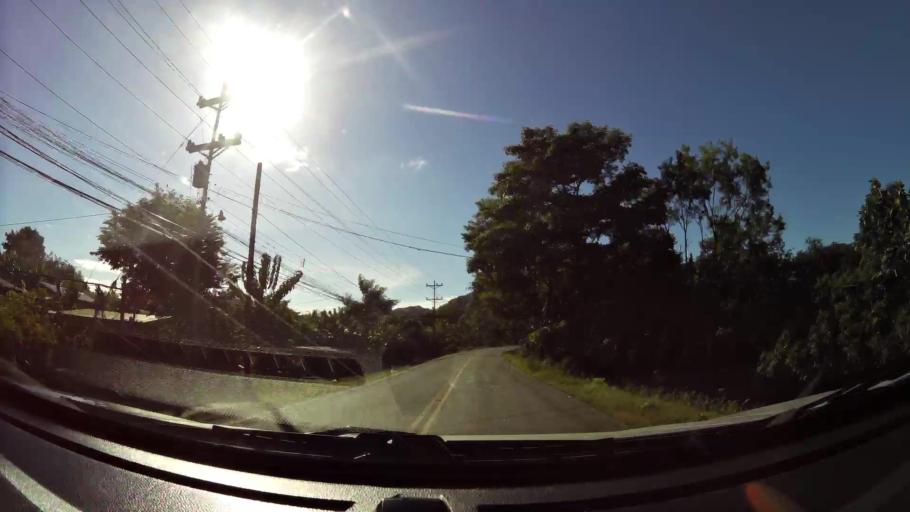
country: CR
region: Guanacaste
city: Belen
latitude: 10.3843
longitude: -85.6200
